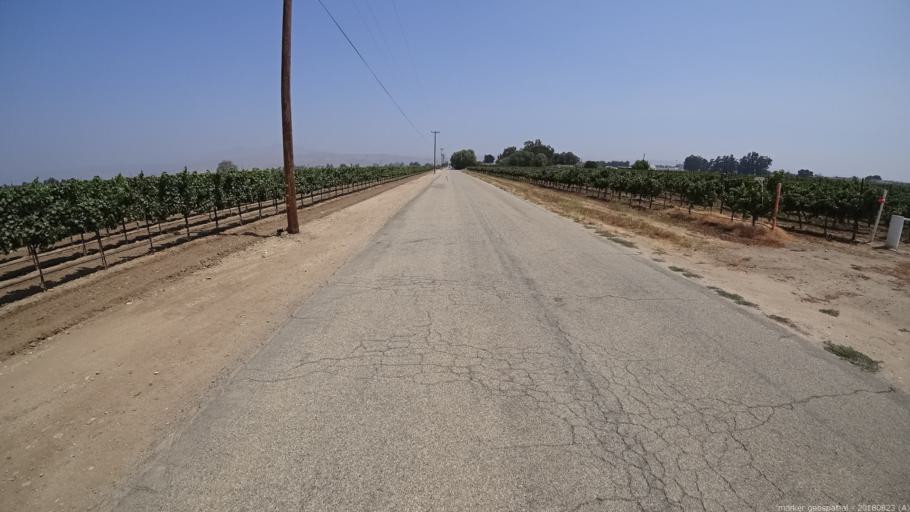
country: US
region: California
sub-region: Monterey County
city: Greenfield
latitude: 36.3266
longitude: -121.2647
